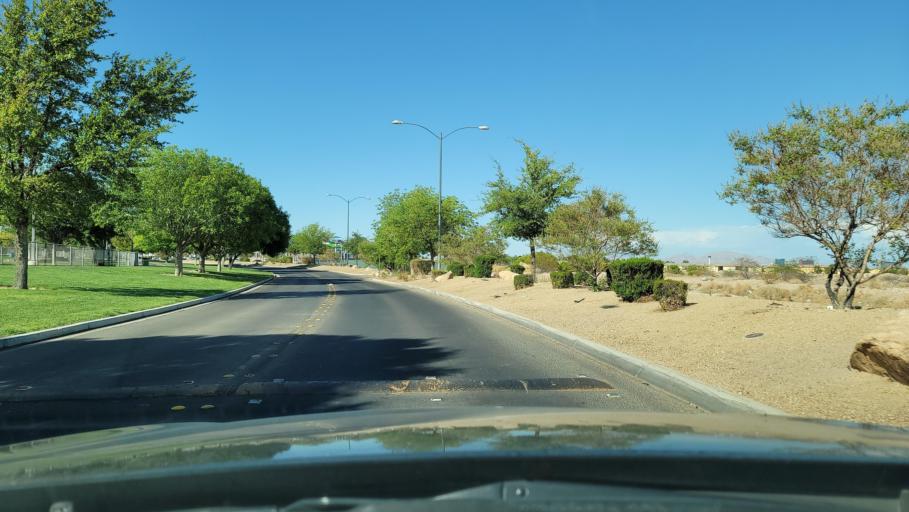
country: US
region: Nevada
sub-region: Clark County
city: Spring Valley
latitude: 36.1223
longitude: -115.2740
